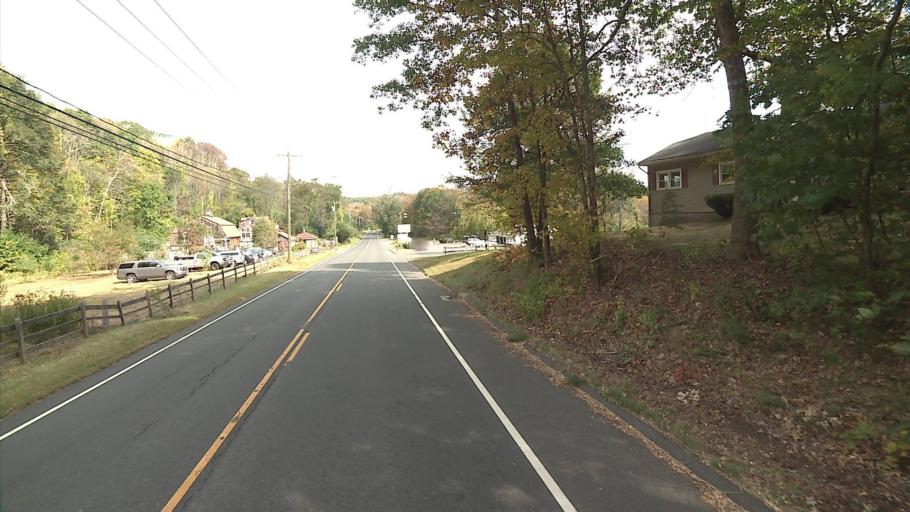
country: US
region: Connecticut
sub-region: Litchfield County
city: Woodbury Center
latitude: 41.5700
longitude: -73.1903
